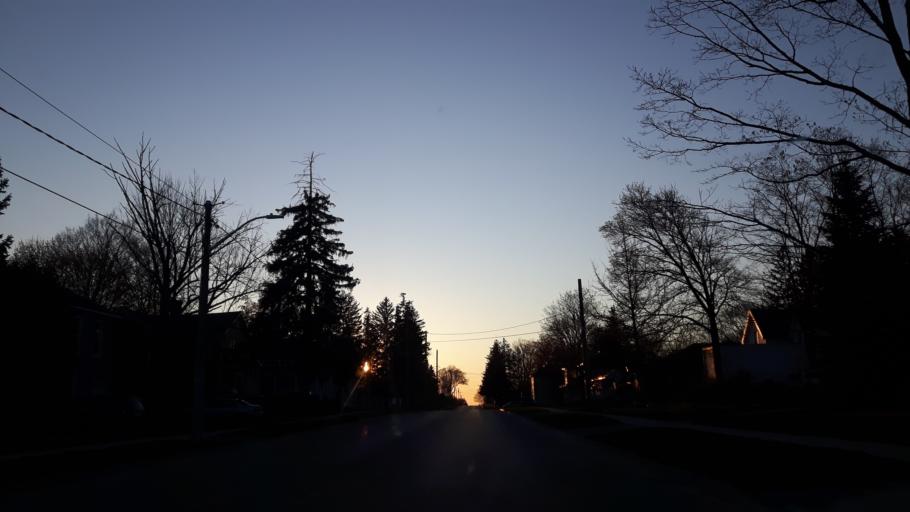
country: CA
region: Ontario
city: Bluewater
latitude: 43.6185
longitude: -81.5427
